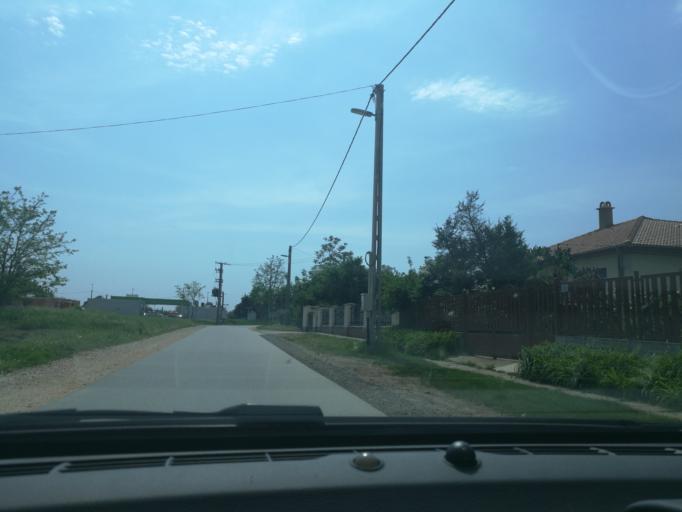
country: HU
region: Szabolcs-Szatmar-Bereg
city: Nyiregyhaza
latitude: 47.9589
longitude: 21.6850
